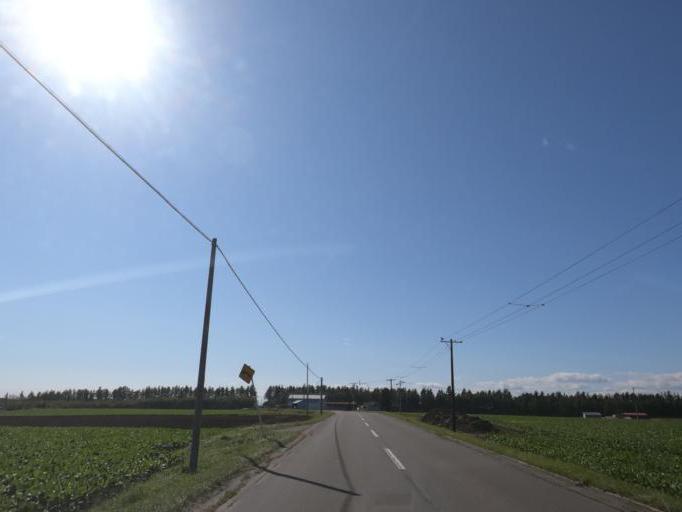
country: JP
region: Hokkaido
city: Obihiro
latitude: 42.8170
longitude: 143.2554
